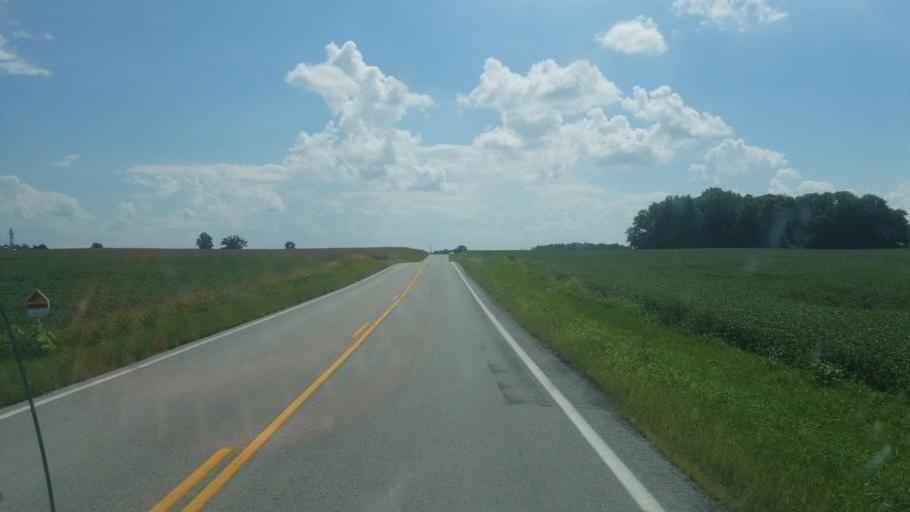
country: US
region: Ohio
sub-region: Hardin County
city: Forest
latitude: 40.8524
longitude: -83.4576
